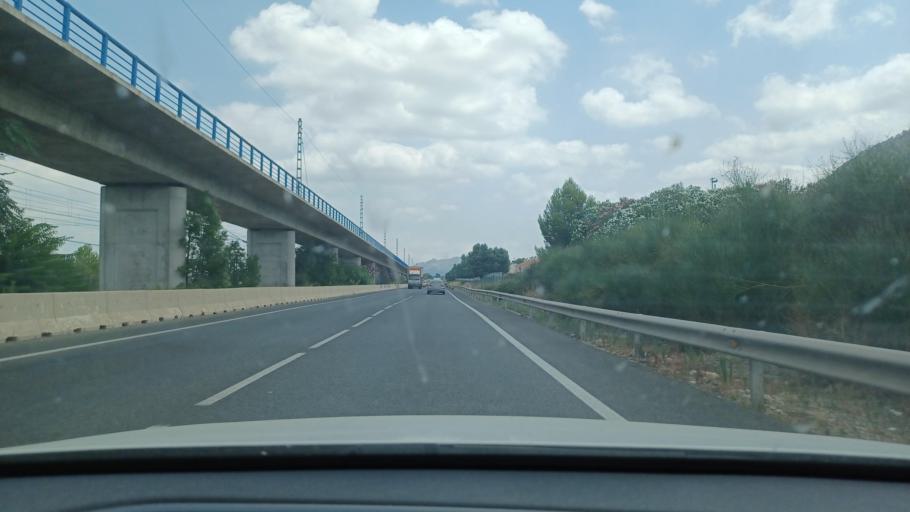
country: ES
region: Valencia
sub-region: Provincia de Valencia
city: Valles
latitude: 38.9805
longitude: -0.5515
